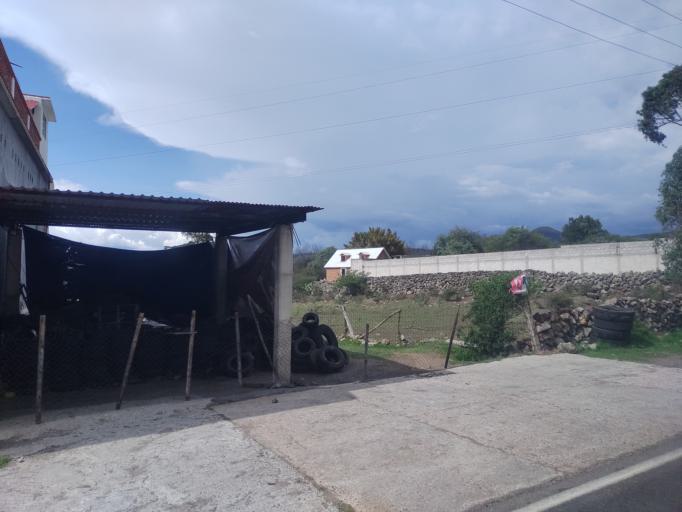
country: MX
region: Mexico
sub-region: Aculco
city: El Colorado
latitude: 20.1064
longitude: -99.7181
